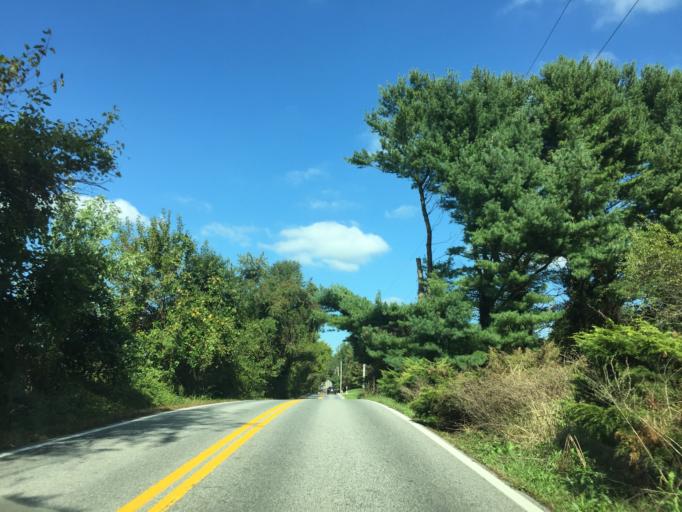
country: US
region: Maryland
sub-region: Harford County
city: Fallston
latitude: 39.4962
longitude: -76.4688
